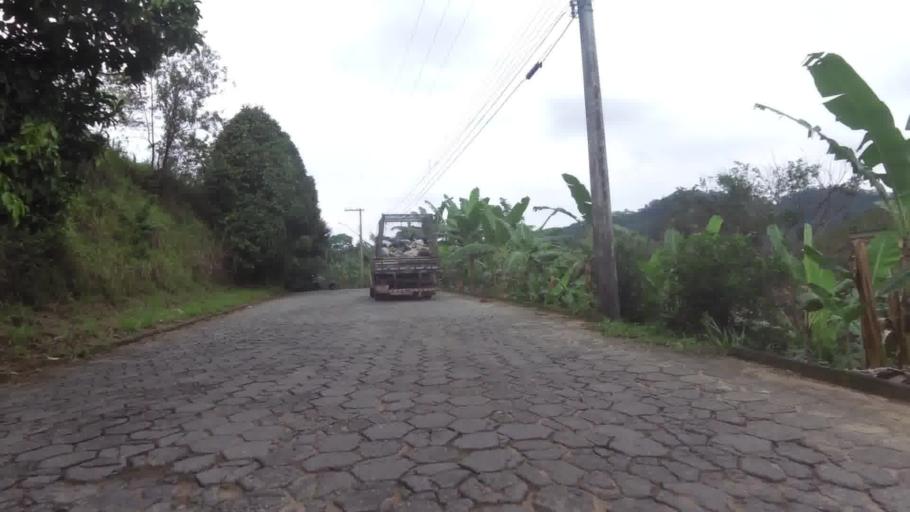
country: BR
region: Espirito Santo
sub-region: Iconha
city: Iconha
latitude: -20.7816
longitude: -40.8256
